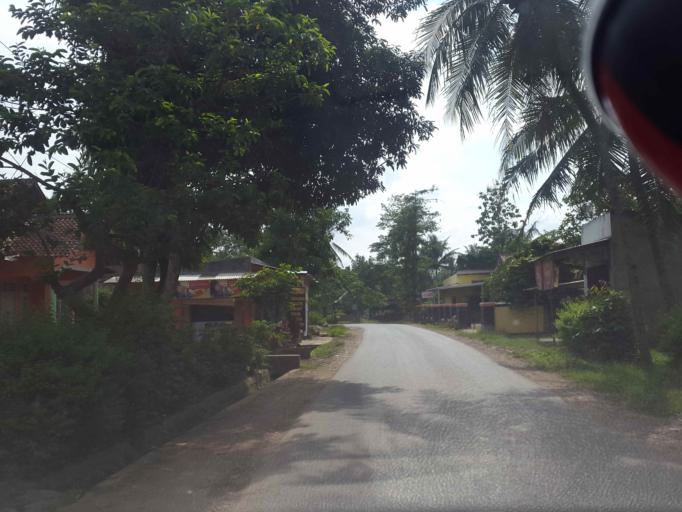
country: ID
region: Lampung
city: Natar
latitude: -5.3089
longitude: 105.2128
